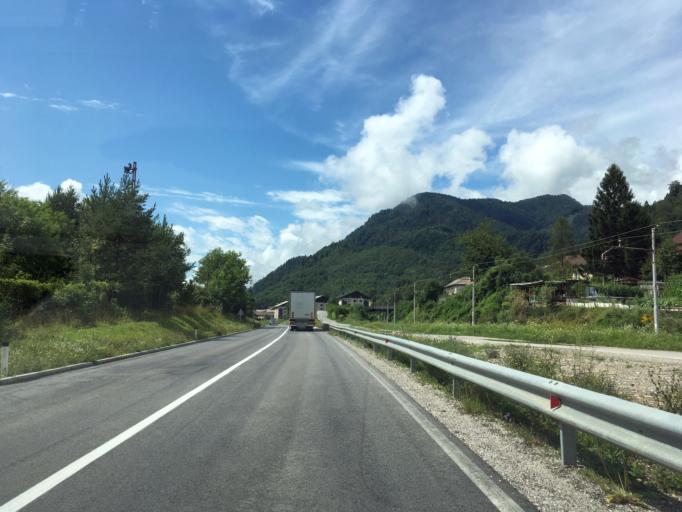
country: SI
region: Jesenice
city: Slovenski Javornik
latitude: 46.4243
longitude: 14.1000
